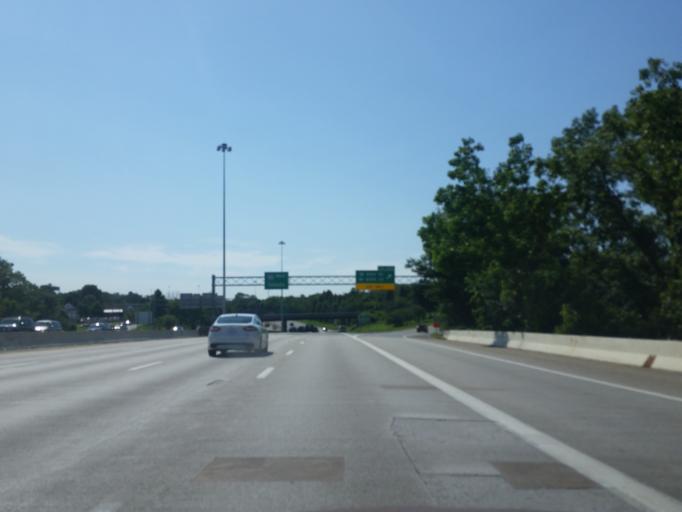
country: US
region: Ohio
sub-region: Cuyahoga County
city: Cleveland
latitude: 41.4744
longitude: -81.7102
